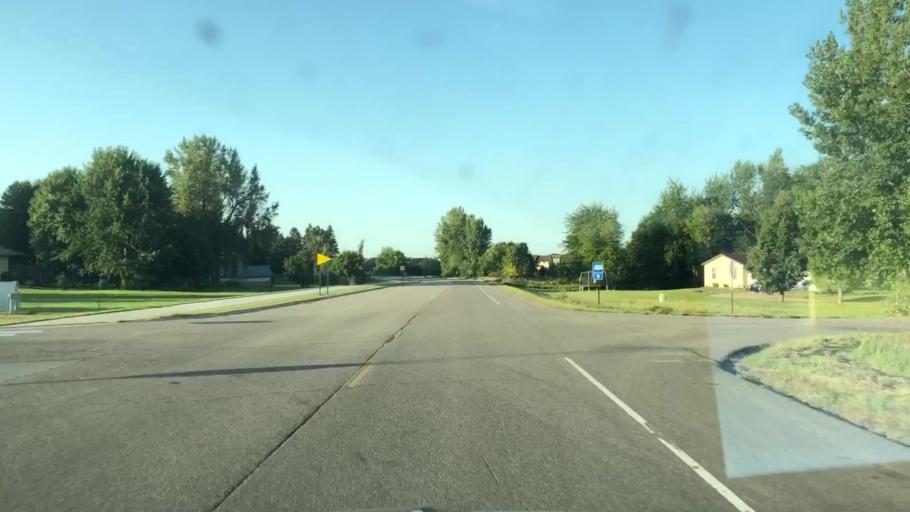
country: US
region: Minnesota
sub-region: Nobles County
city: Worthington
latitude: 43.6166
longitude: -95.6356
